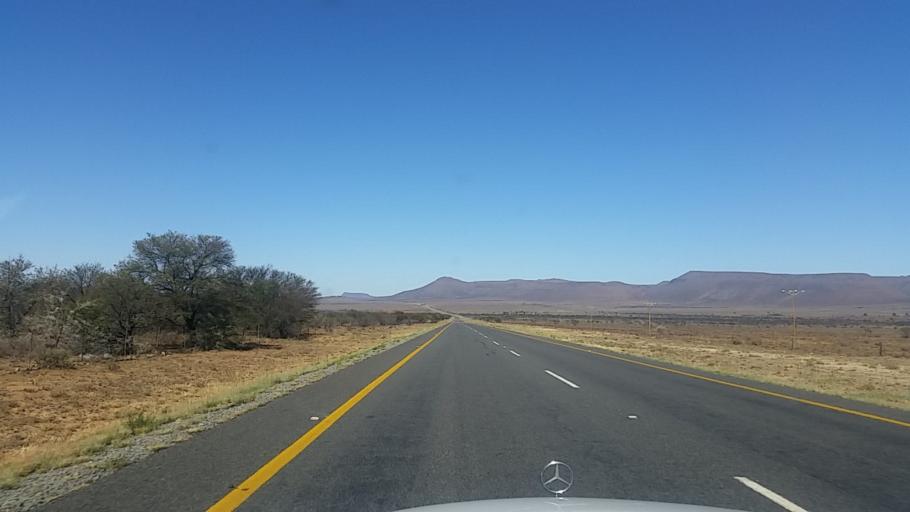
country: ZA
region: Eastern Cape
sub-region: Cacadu District Municipality
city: Graaff-Reinet
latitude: -31.9897
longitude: 24.6854
